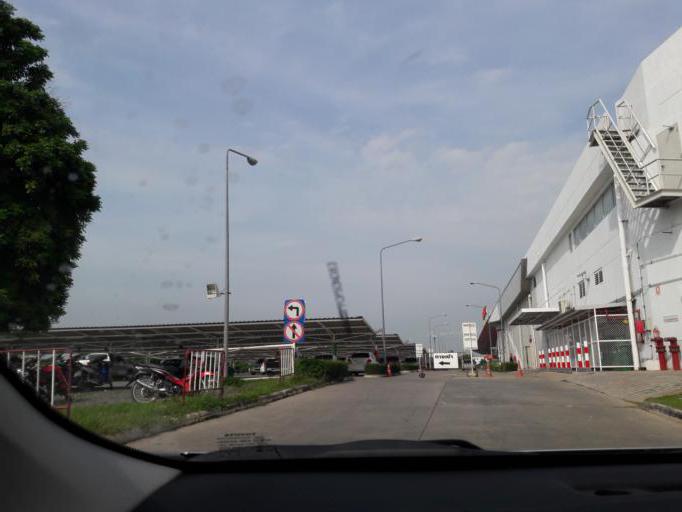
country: TH
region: Ang Thong
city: Ang Thong
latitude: 14.5802
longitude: 100.4587
